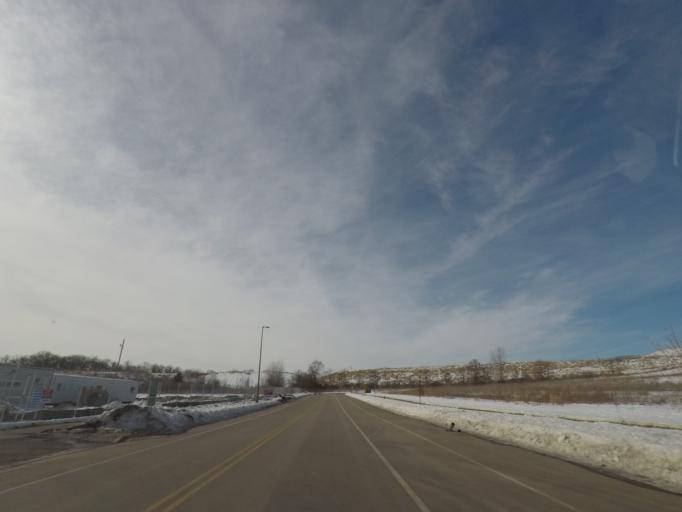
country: US
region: Wisconsin
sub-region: Dane County
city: Fitchburg
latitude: 43.0048
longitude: -89.4687
